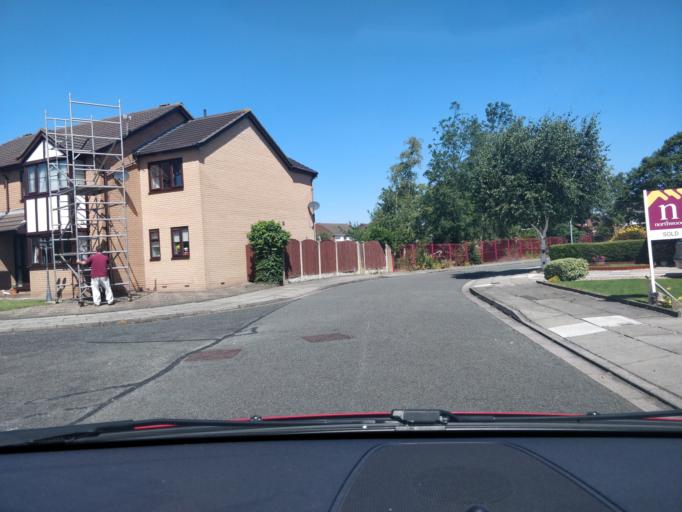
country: GB
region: England
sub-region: Lancashire
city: Banks
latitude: 53.6737
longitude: -2.9458
